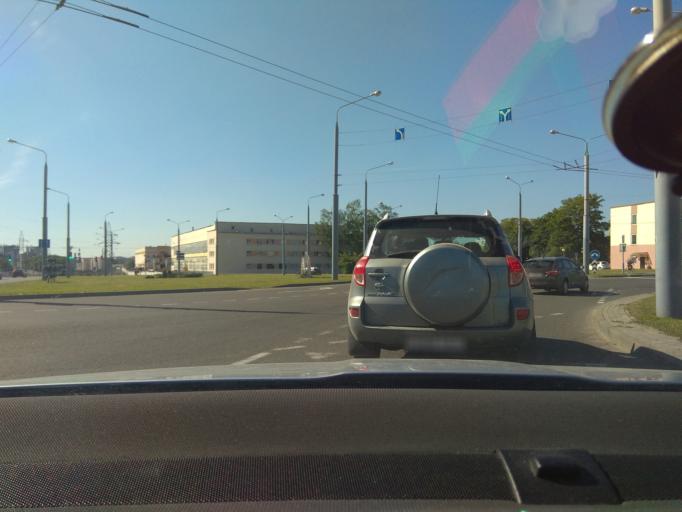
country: BY
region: Grodnenskaya
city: Hrodna
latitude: 53.6529
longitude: 23.7939
